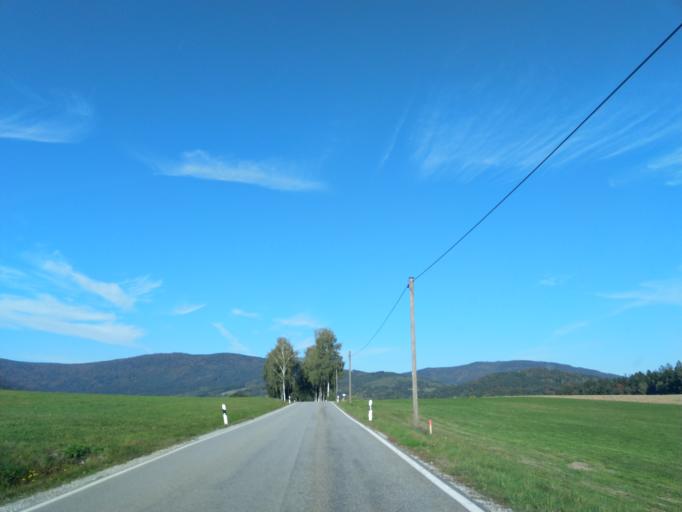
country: DE
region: Bavaria
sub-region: Lower Bavaria
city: Bernried
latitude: 48.9014
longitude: 12.8690
